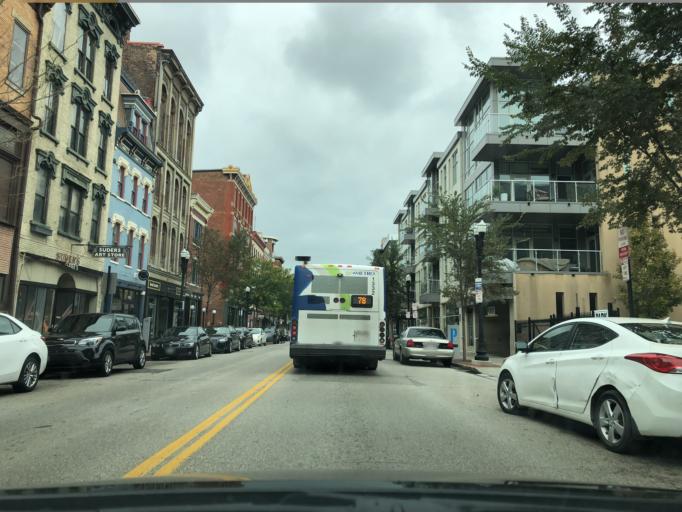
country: US
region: Kentucky
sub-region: Campbell County
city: Newport
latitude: 39.1095
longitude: -84.5151
